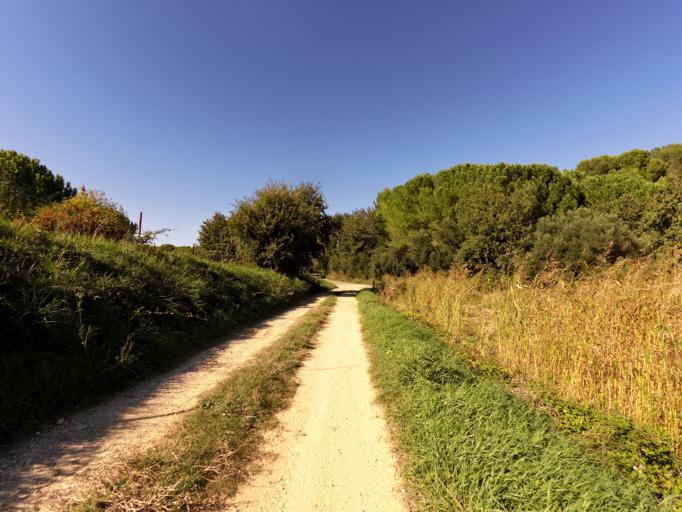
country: FR
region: Languedoc-Roussillon
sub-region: Departement du Gard
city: Aigues-Vives
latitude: 43.7327
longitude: 4.1776
